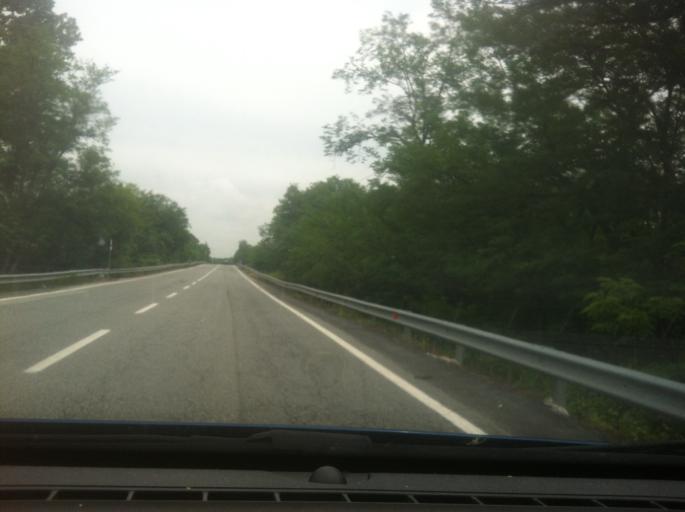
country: IT
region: Piedmont
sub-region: Provincia di Torino
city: San Benigno Canavese
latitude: 45.2453
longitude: 7.8032
